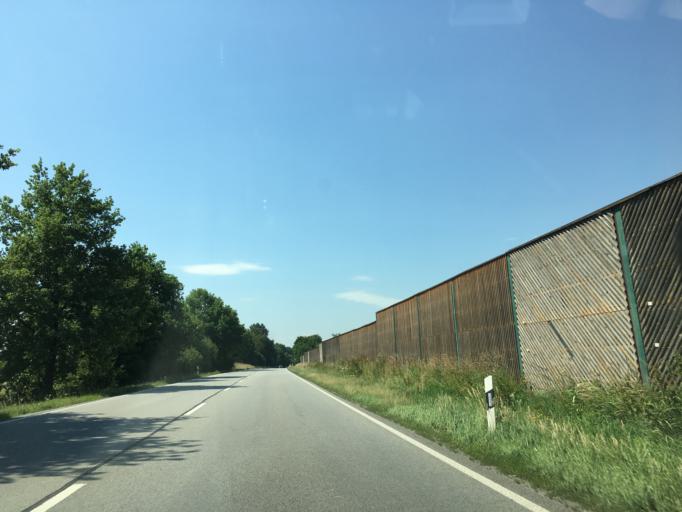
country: DE
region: Bavaria
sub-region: Upper Bavaria
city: Edling
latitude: 48.0531
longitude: 12.1918
